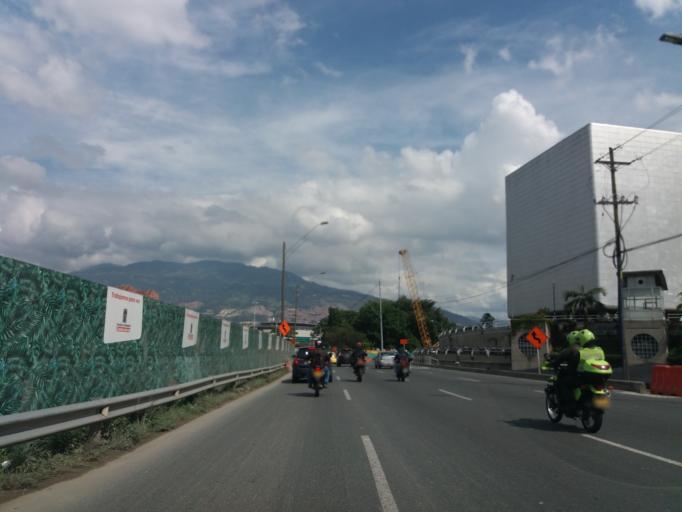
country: CO
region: Antioquia
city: Medellin
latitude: 6.2453
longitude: -75.5786
